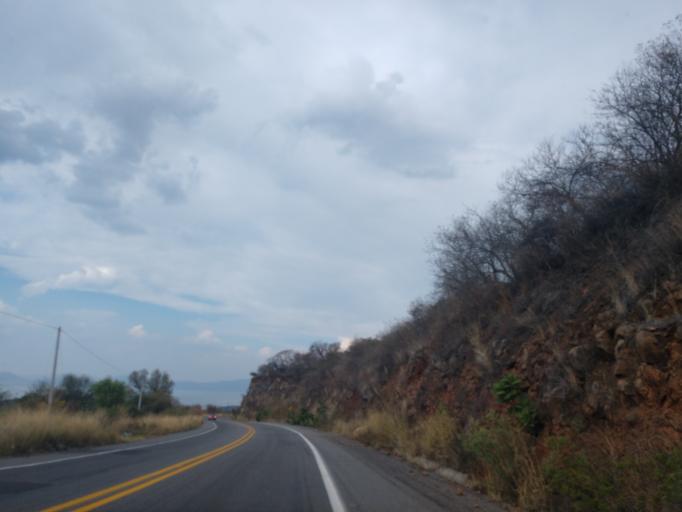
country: MX
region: Jalisco
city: La Manzanilla de la Paz
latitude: 20.1020
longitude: -103.1713
